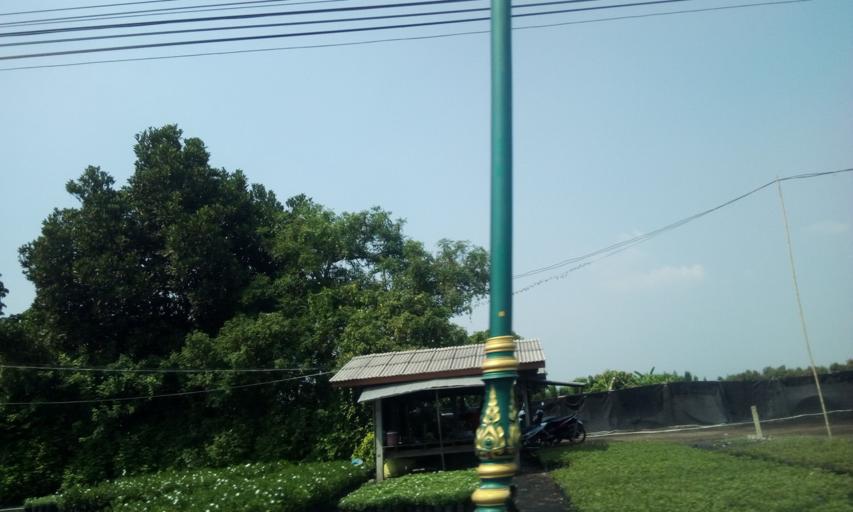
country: TH
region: Nakhon Nayok
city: Ongkharak
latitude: 14.1399
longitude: 100.9707
